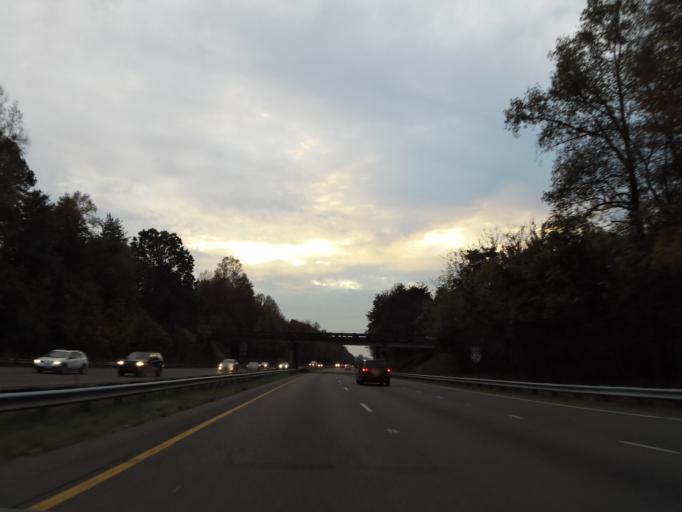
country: US
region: North Carolina
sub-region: Burke County
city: Drexel
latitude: 35.7286
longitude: -81.6162
